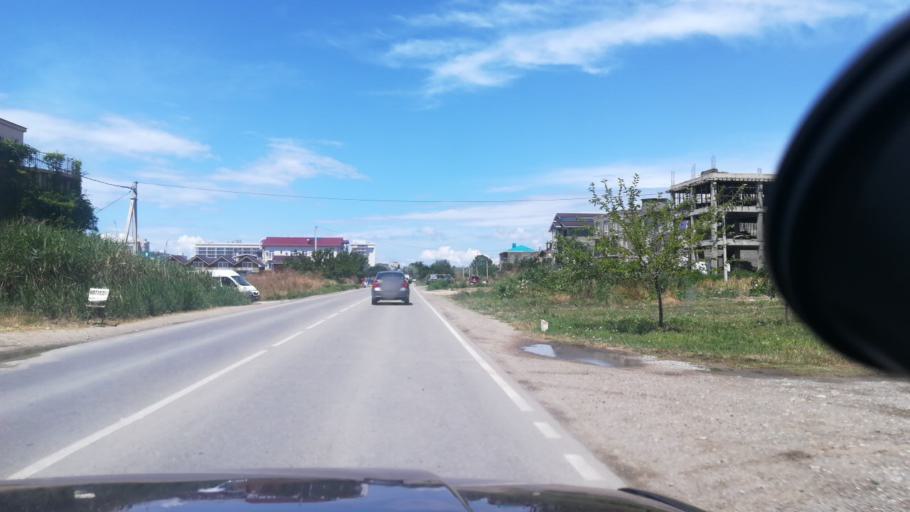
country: RU
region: Krasnodarskiy
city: Vityazevo
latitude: 44.9618
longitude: 37.2933
